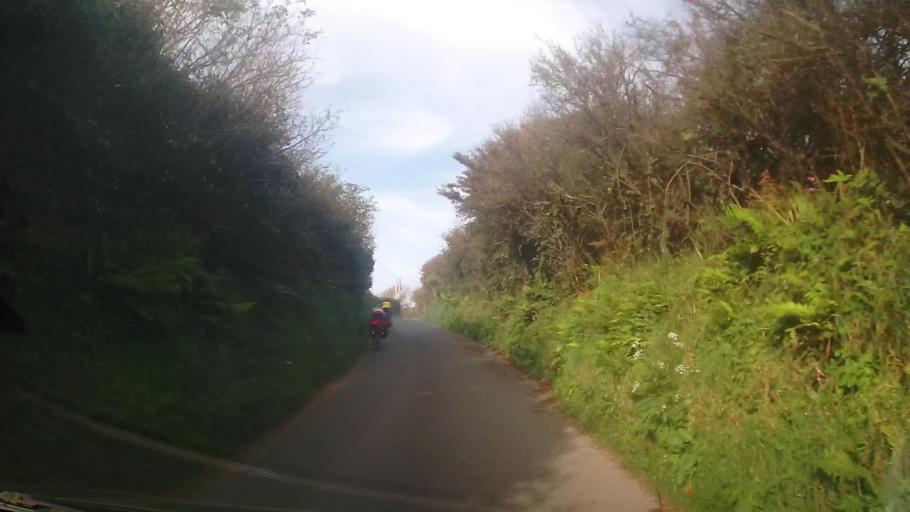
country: GB
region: Wales
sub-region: Pembrokeshire
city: Camrose
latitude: 51.8548
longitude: -5.0558
